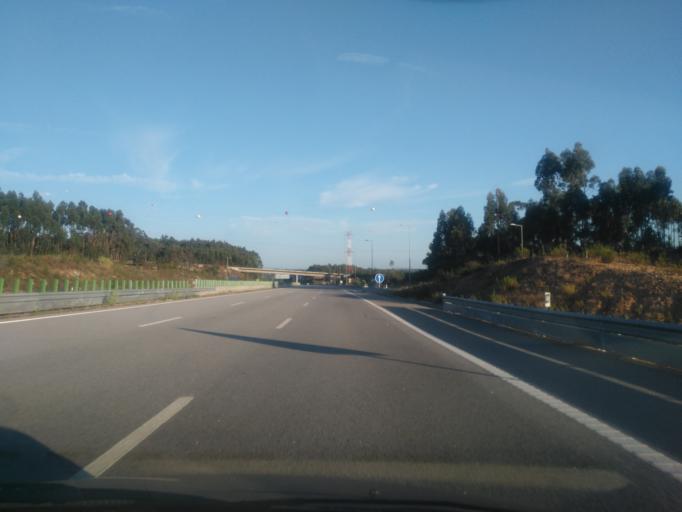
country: PT
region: Coimbra
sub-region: Figueira da Foz
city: Alhadas
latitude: 40.1585
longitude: -8.7759
